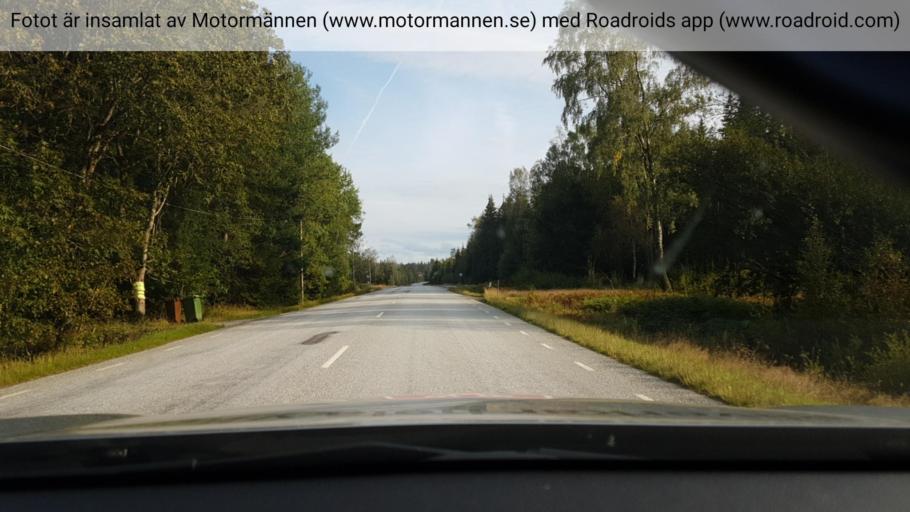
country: SE
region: Vaestra Goetaland
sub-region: Uddevalla Kommun
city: Ljungskile
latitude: 58.1659
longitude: 11.9672
